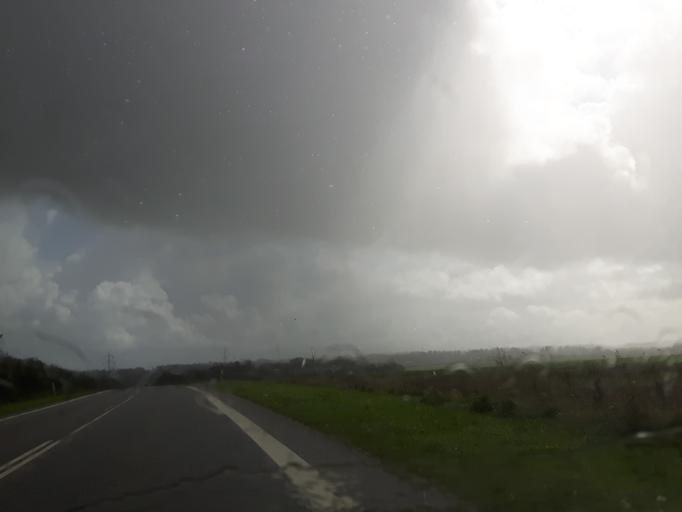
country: DK
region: Central Jutland
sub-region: Struer Kommune
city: Struer
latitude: 56.6281
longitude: 8.5142
